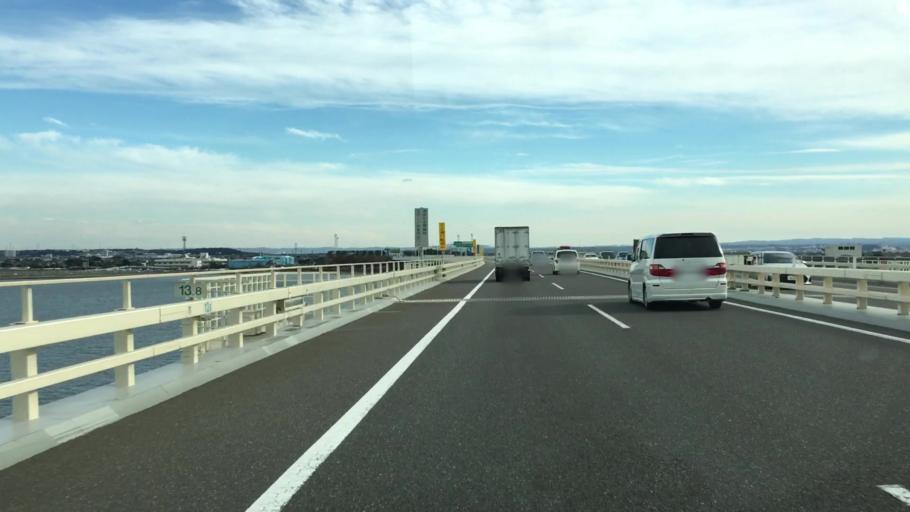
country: JP
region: Chiba
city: Kisarazu
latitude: 35.4404
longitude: 139.9096
